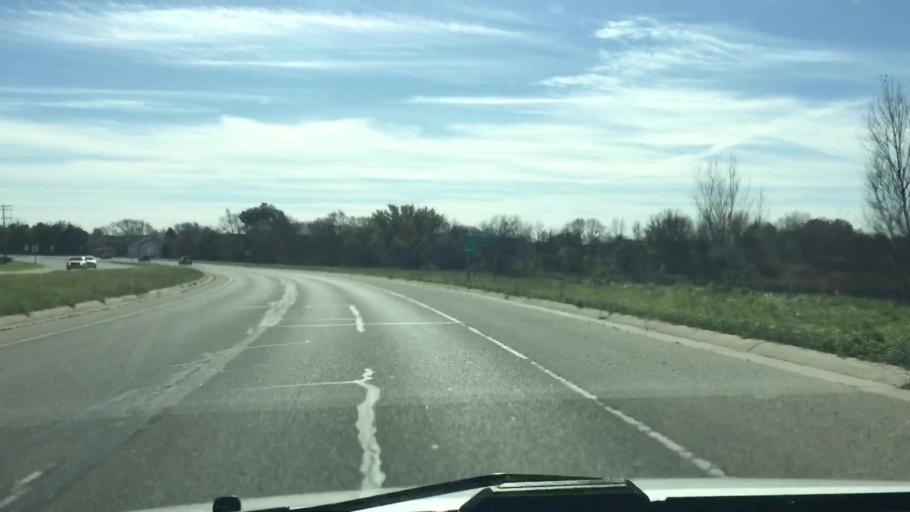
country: US
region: Wisconsin
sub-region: Waukesha County
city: Pewaukee
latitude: 43.0965
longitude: -88.2439
